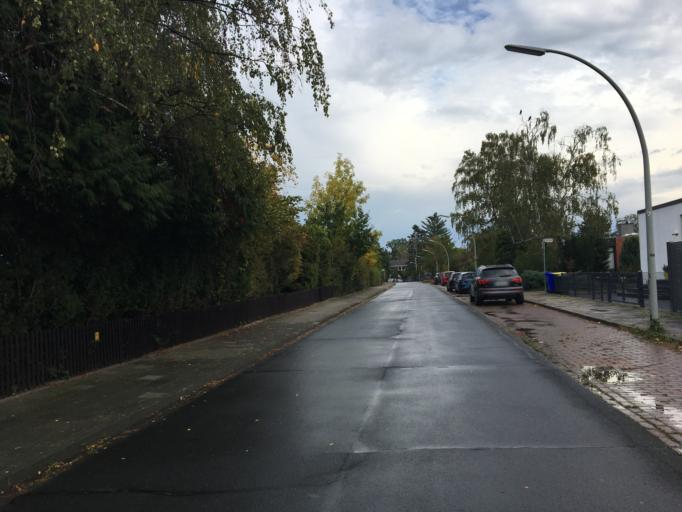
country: DE
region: Lower Saxony
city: Braunschweig
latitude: 52.3013
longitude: 10.5705
